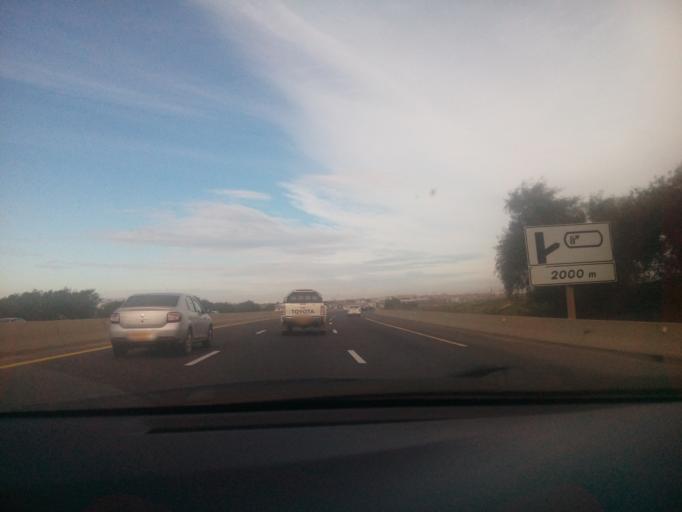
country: DZ
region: Oran
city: Es Senia
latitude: 35.5832
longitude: -0.5709
